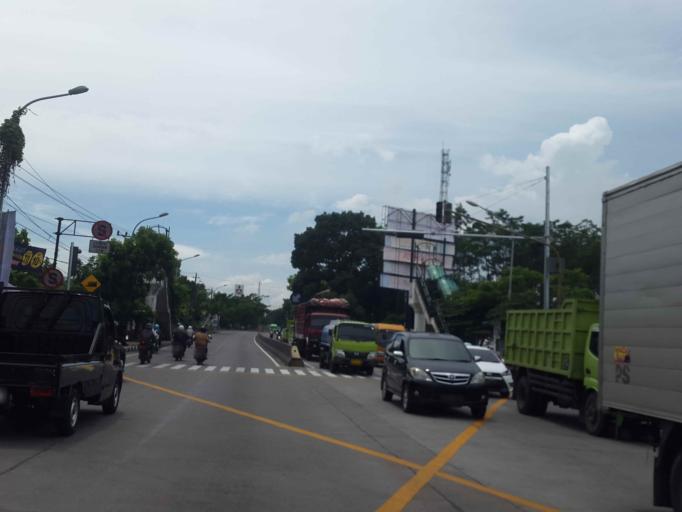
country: ID
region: Central Java
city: Ungaran
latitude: -7.0731
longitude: 110.4111
